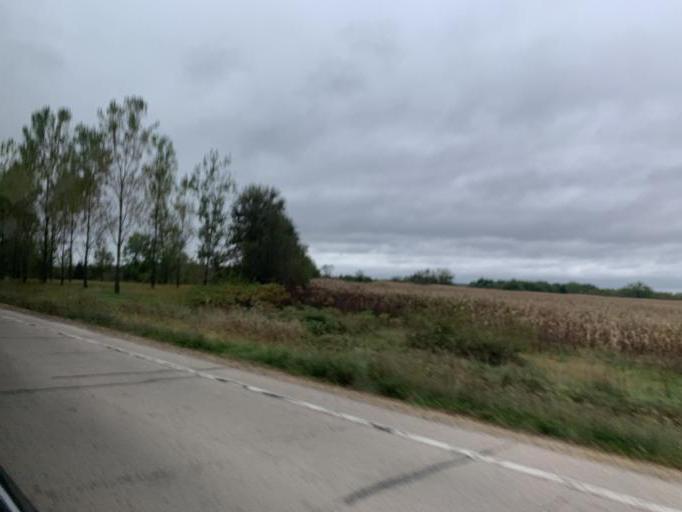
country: US
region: Wisconsin
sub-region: Grant County
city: Muscoda
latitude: 43.2086
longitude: -90.4560
